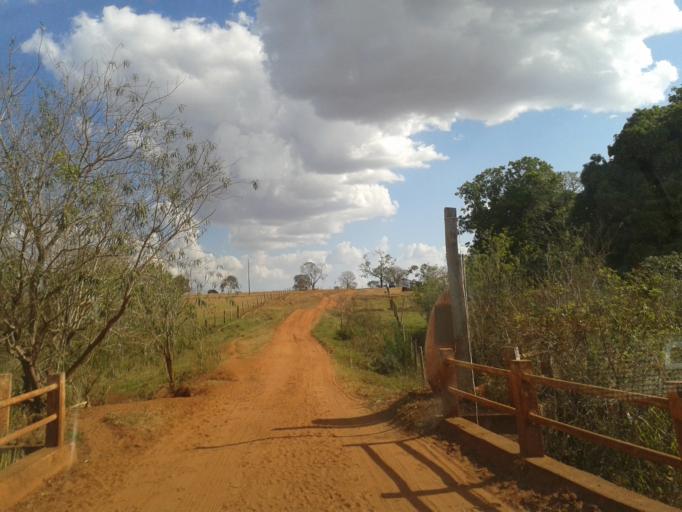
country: BR
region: Minas Gerais
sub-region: Santa Vitoria
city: Santa Vitoria
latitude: -19.2723
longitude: -49.9918
